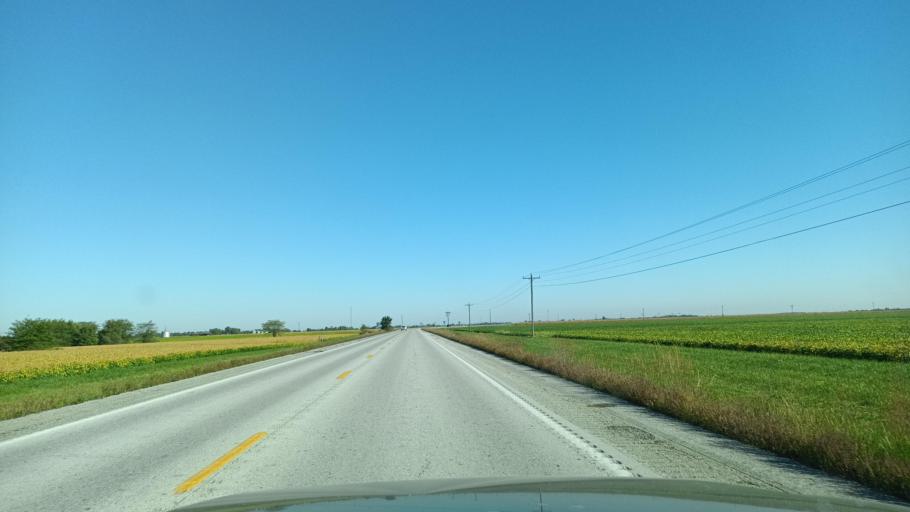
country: US
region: Missouri
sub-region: Audrain County
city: Vandalia
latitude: 39.4064
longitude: -91.6415
